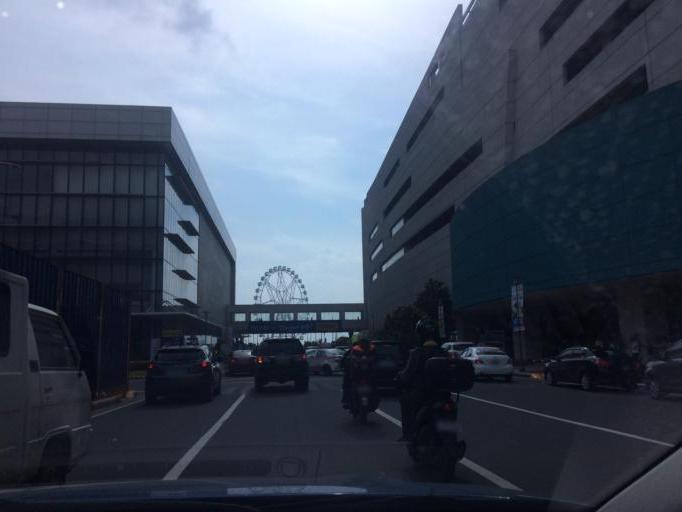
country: PH
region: Metro Manila
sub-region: City of Manila
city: Port Area
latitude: 14.5330
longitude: 120.9824
